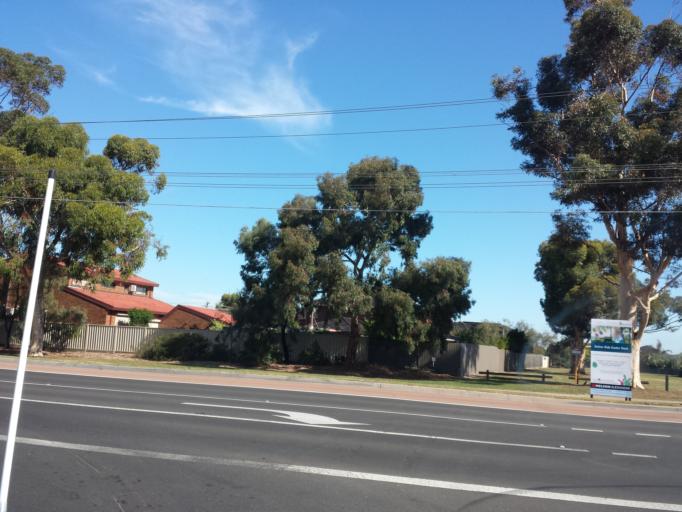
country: AU
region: Victoria
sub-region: Moonee Valley
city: Essendon West
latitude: -37.7517
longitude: 144.8712
